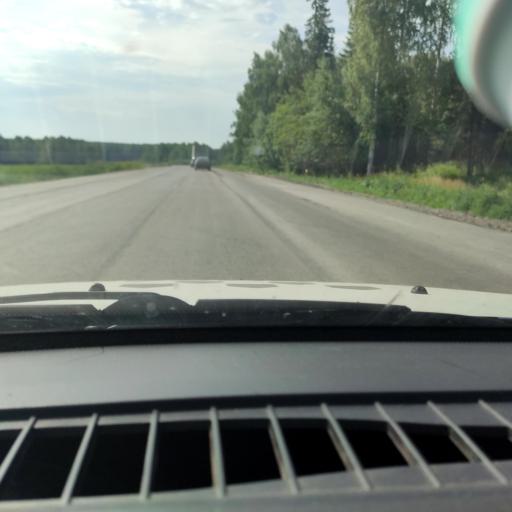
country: RU
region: Perm
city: Siva
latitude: 58.4612
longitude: 54.4079
